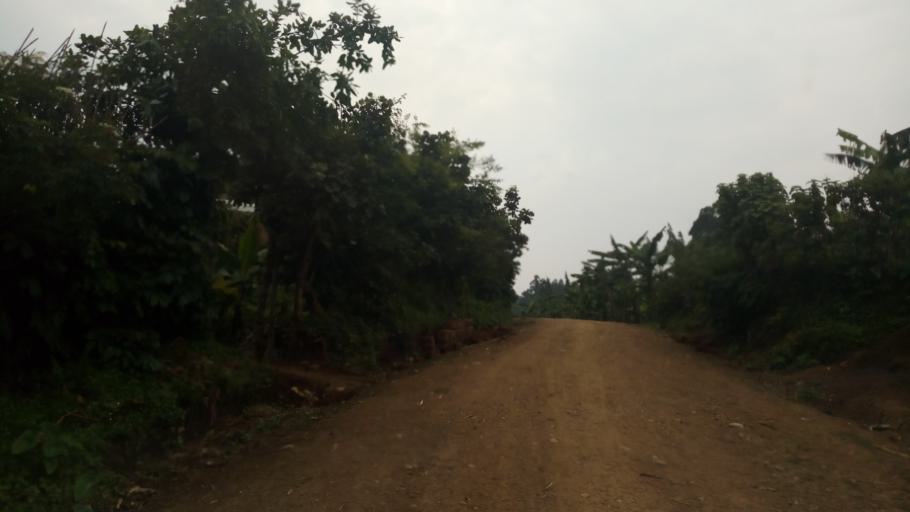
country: UG
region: Western Region
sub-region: Kisoro District
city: Kisoro
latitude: -1.2579
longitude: 29.6303
